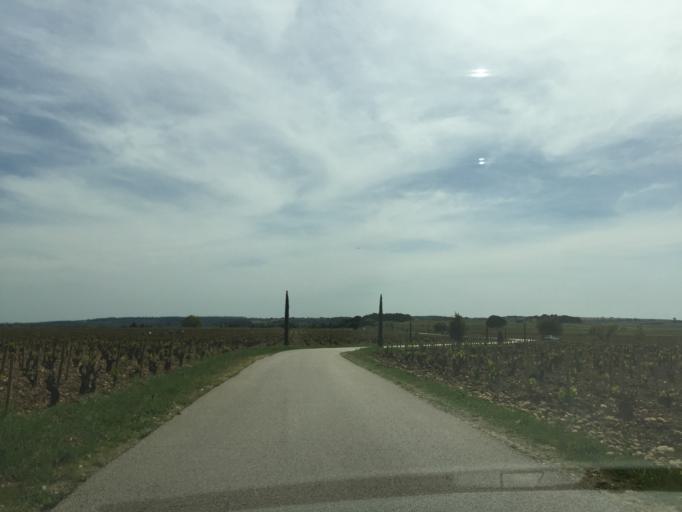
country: FR
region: Provence-Alpes-Cote d'Azur
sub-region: Departement du Vaucluse
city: Courthezon
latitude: 44.1046
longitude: 4.8531
